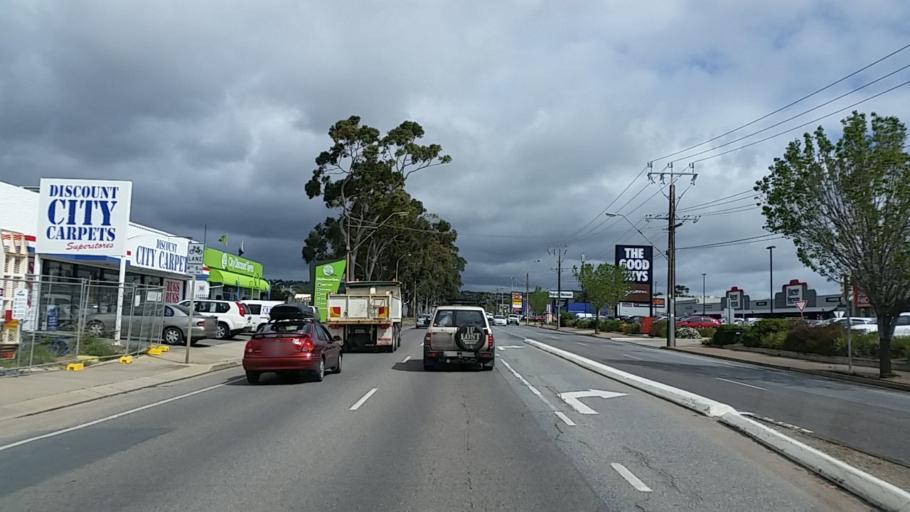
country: AU
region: South Australia
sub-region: Marion
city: Sturt
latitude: -35.0103
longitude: 138.5583
